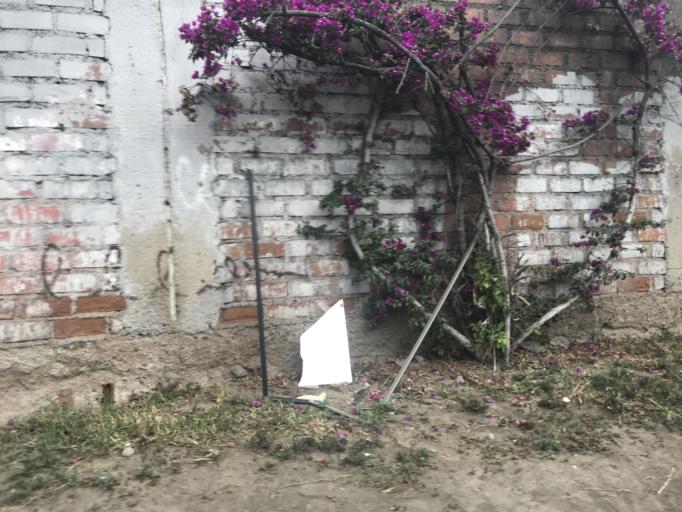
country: PE
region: Callao
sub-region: Callao
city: Callao
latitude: -12.0688
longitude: -77.0912
